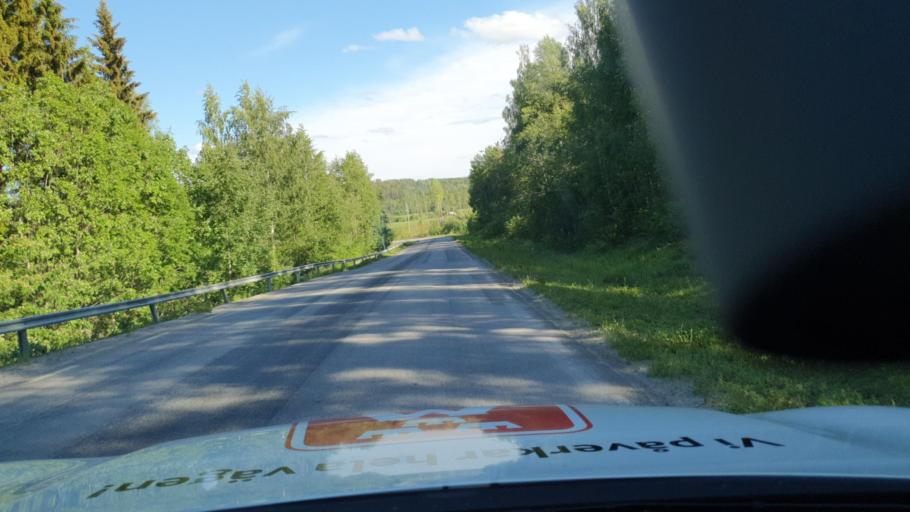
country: SE
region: Vaesterbotten
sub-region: Vannas Kommun
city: Vaennaes
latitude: 63.8911
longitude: 19.7057
